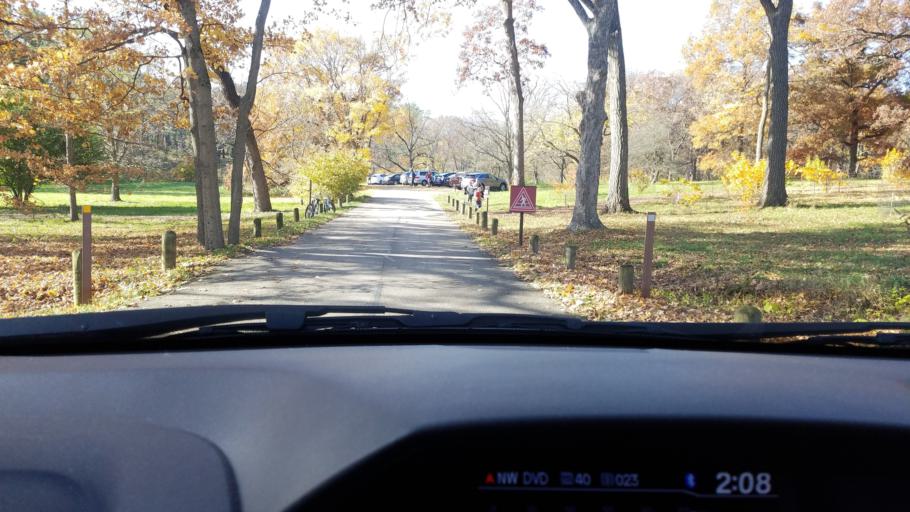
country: US
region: Illinois
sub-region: DuPage County
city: Lisle
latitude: 41.8167
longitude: -88.0829
